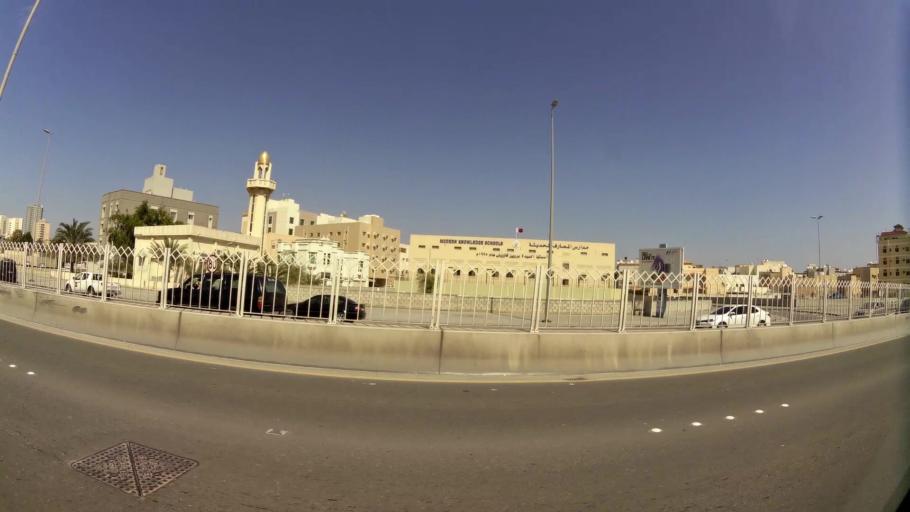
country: BH
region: Manama
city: Manama
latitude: 26.2058
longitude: 50.5995
